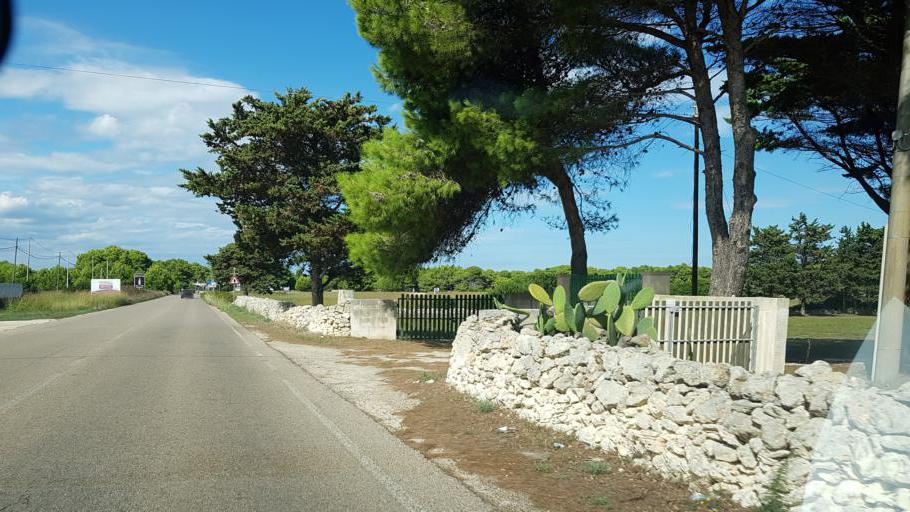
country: IT
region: Apulia
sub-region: Provincia di Lecce
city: Borgagne
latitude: 40.2634
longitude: 18.4331
